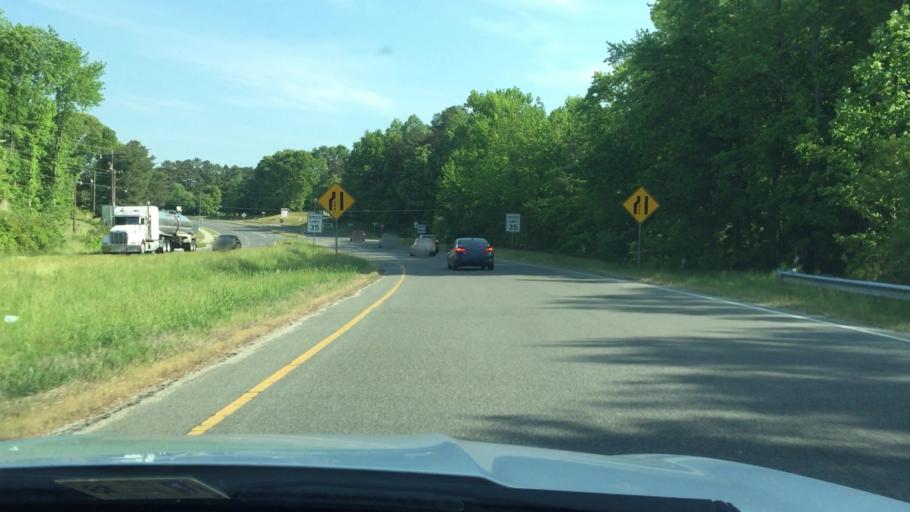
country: US
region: Virginia
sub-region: Lancaster County
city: Kilmarnock
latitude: 37.6974
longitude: -76.3737
